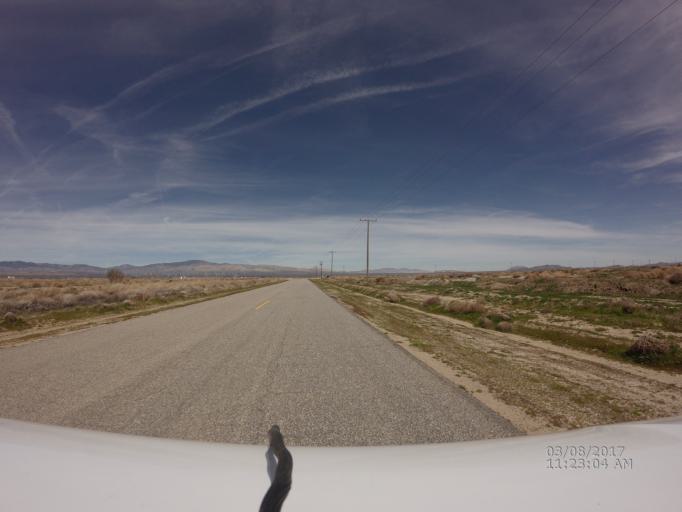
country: US
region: California
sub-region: Los Angeles County
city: Green Valley
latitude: 34.8023
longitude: -118.3790
